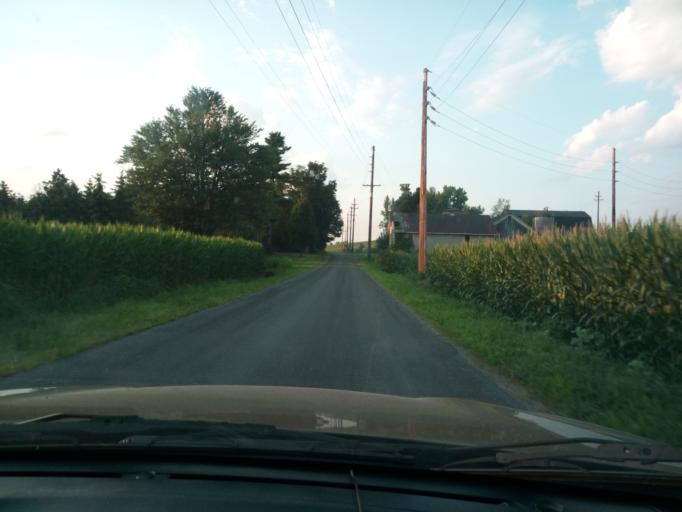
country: US
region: New York
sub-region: Wayne County
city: Clyde
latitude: 43.0641
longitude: -76.8326
